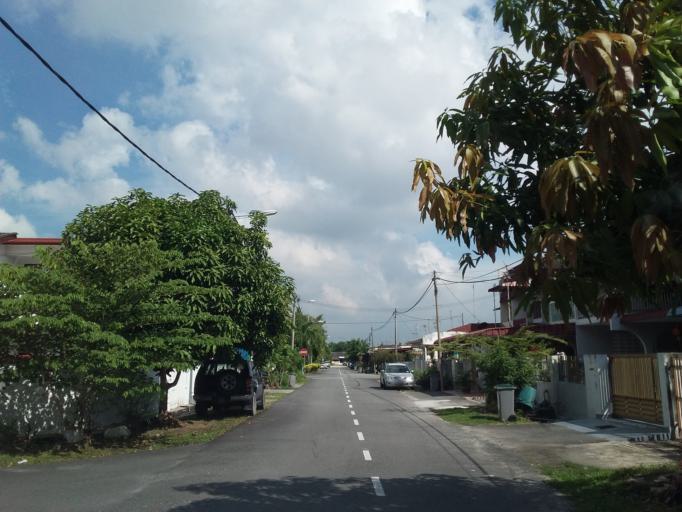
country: MY
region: Johor
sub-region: Daerah Batu Pahat
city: Batu Pahat
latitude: 1.8406
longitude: 102.9285
